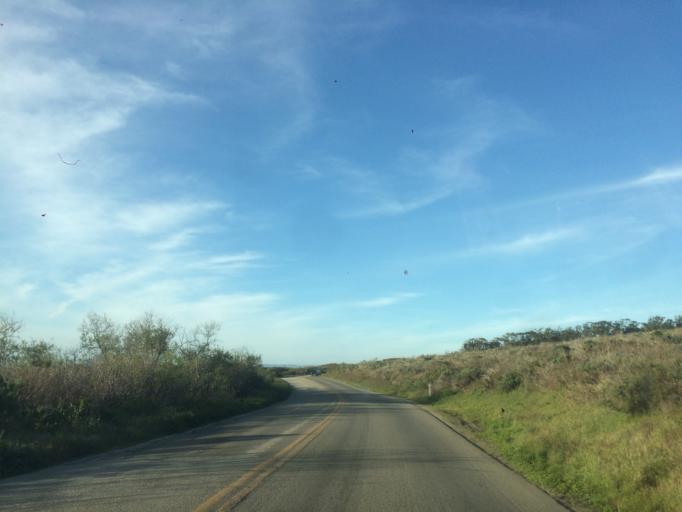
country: US
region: California
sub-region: San Luis Obispo County
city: Los Osos
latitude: 35.2805
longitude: -120.8830
